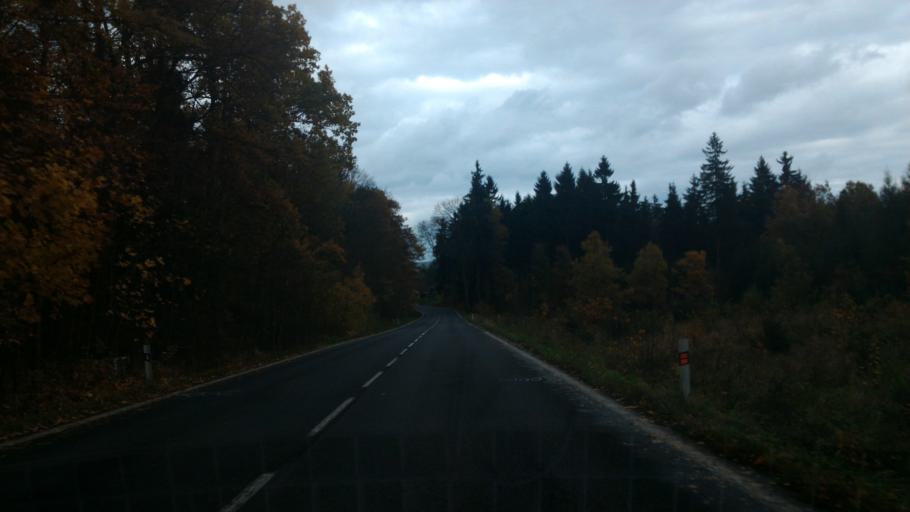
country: CZ
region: Ustecky
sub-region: Okres Decin
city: Rumburk
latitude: 50.9703
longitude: 14.5645
